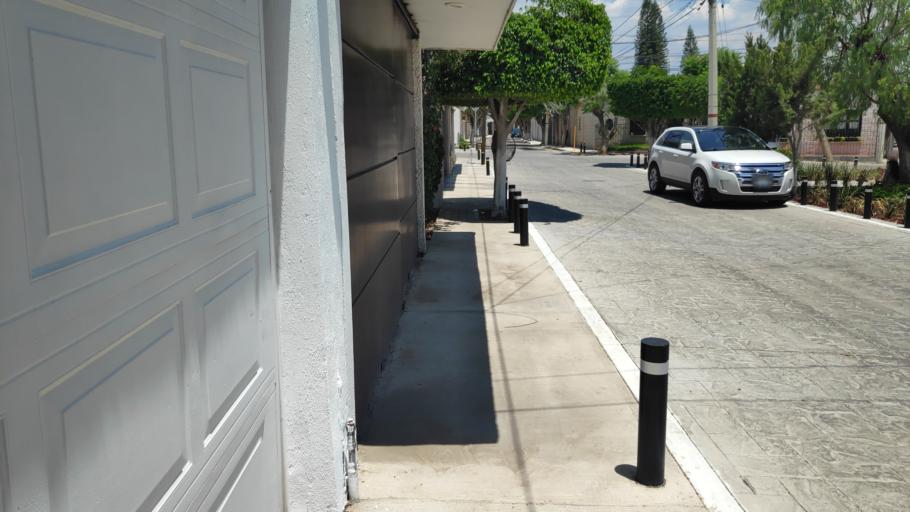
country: MX
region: Queretaro
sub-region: Queretaro
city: Santiago de Queretaro
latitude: 20.6131
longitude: -100.3869
